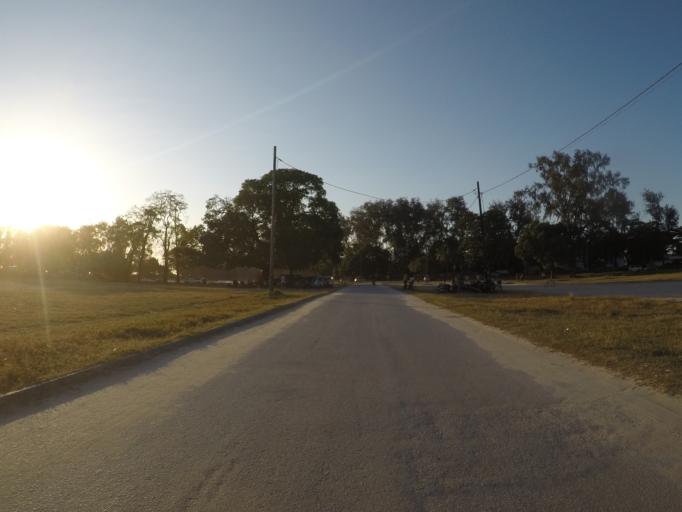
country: TZ
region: Zanzibar Urban/West
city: Zanzibar
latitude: -6.1740
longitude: 39.1964
